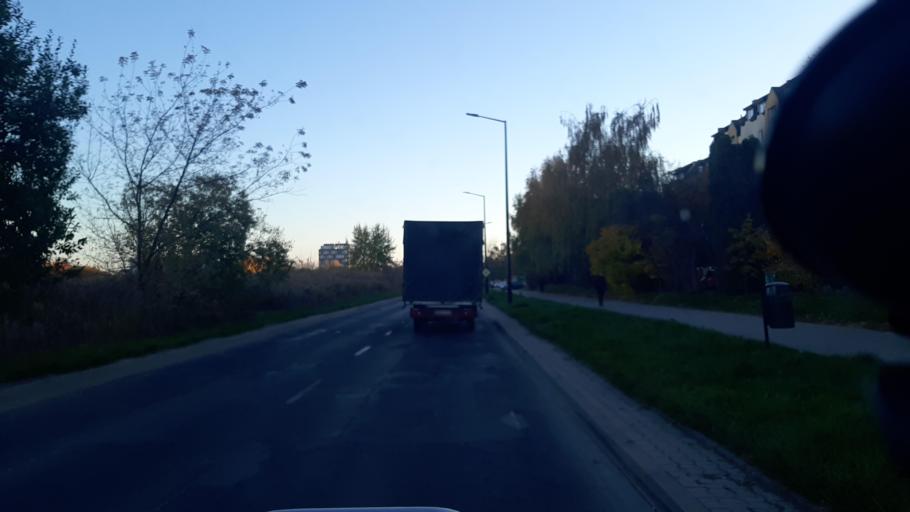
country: PL
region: Lublin Voivodeship
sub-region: Powiat lubelski
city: Lublin
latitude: 51.2602
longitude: 22.5584
